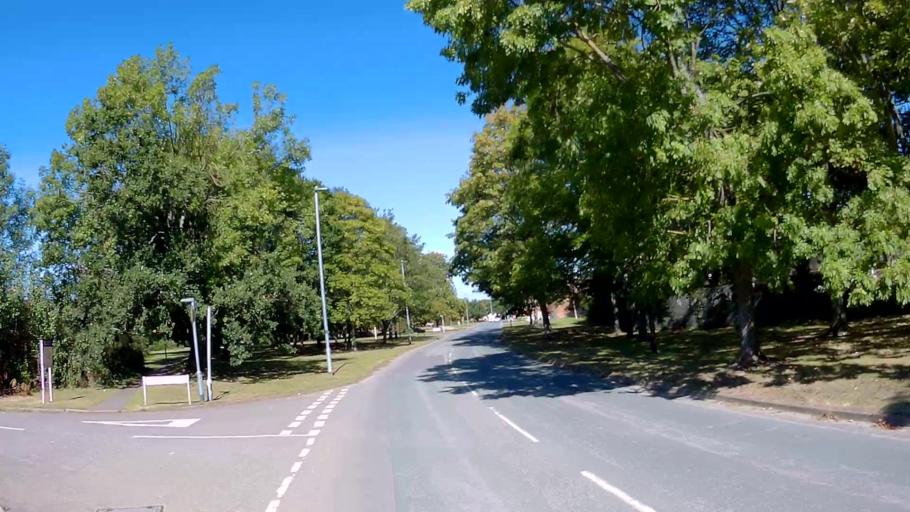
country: GB
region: England
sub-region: West Berkshire
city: Arborfield
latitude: 51.3820
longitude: -0.9000
